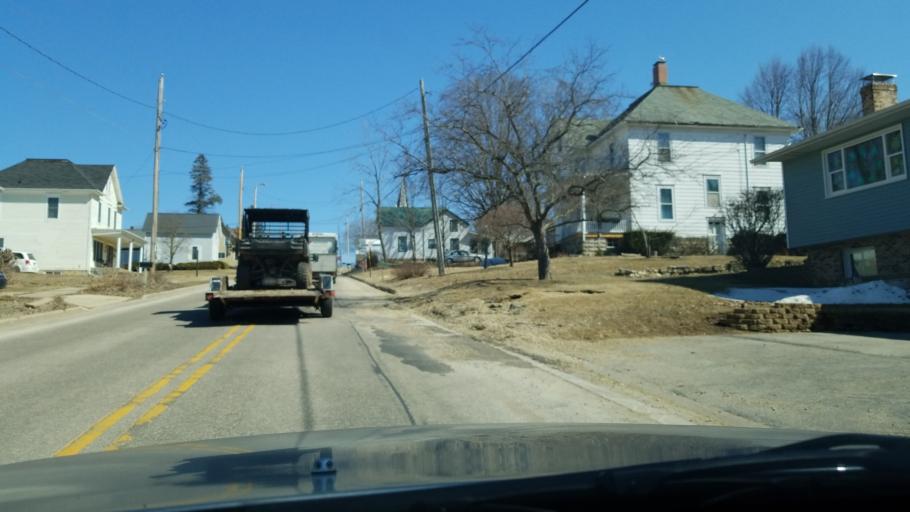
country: US
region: Wisconsin
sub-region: Iowa County
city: Mineral Point
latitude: 42.8606
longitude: -90.1902
